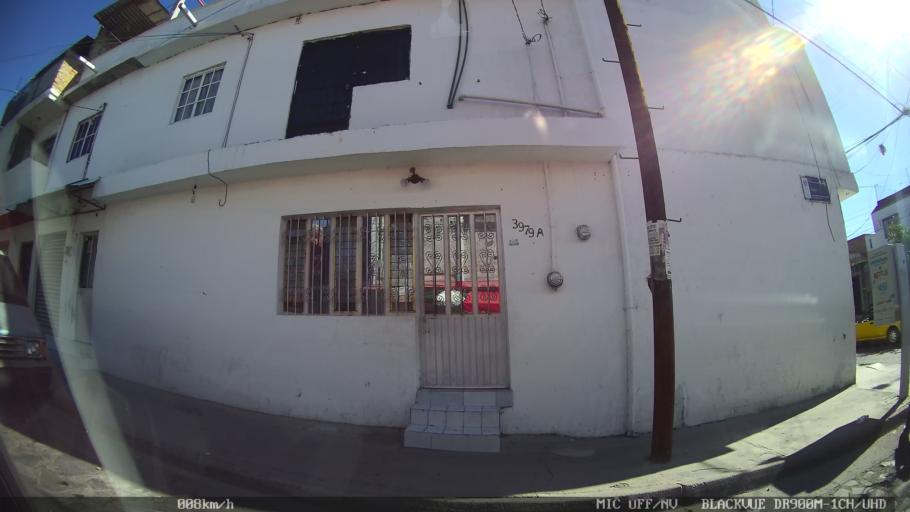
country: MX
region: Jalisco
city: Tlaquepaque
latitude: 20.6892
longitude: -103.2724
